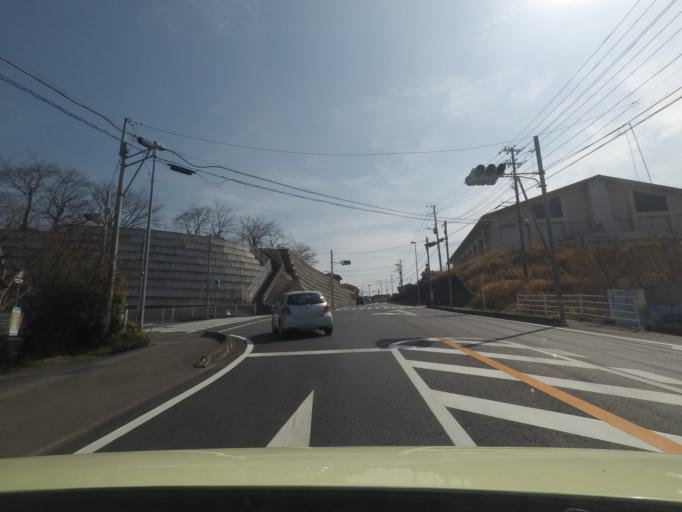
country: JP
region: Ibaraki
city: Ishioka
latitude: 36.1691
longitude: 140.3585
